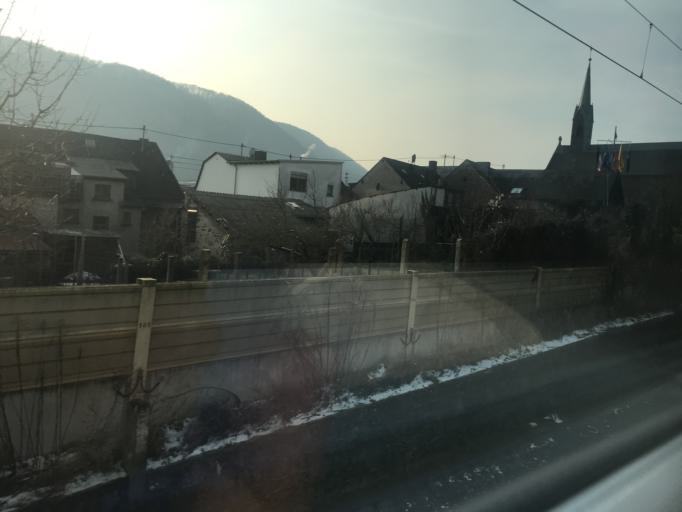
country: DE
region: Rheinland-Pfalz
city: Hatzenport
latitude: 50.2286
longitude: 7.4197
